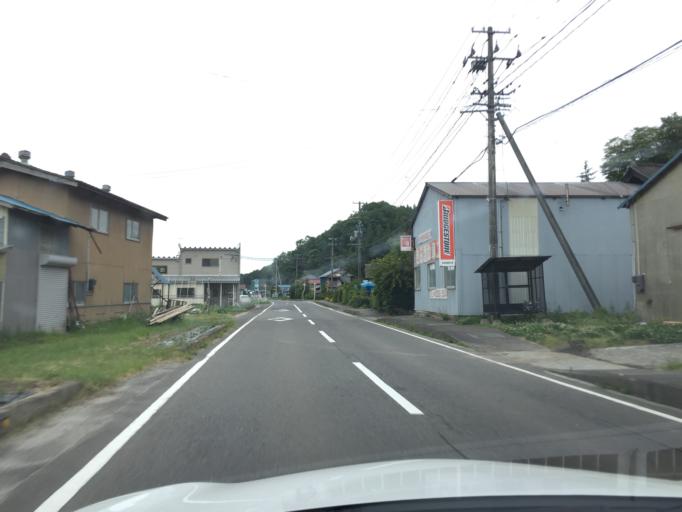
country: JP
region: Fukushima
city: Funehikimachi-funehiki
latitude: 37.3171
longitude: 140.6599
